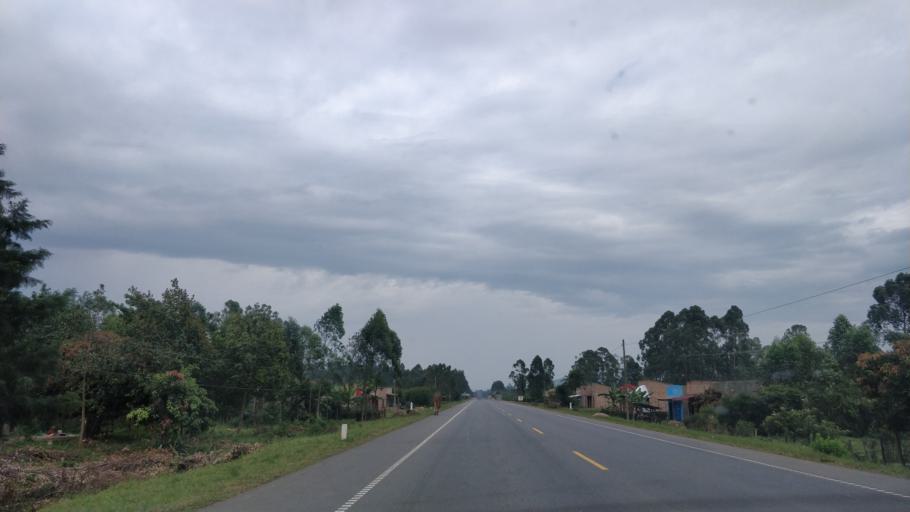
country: UG
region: Western Region
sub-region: Sheema District
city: Kibingo
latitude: -0.6725
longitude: 30.4288
